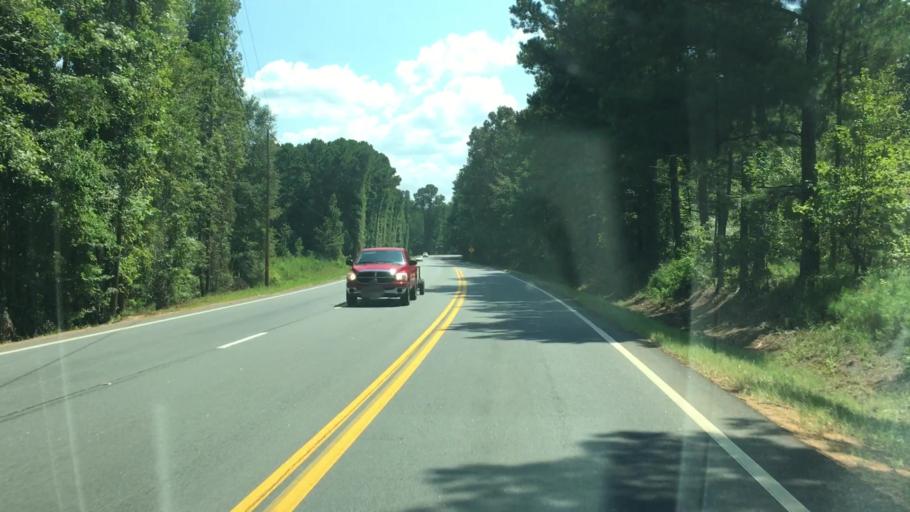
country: US
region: Georgia
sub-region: Oconee County
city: Watkinsville
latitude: 33.7309
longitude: -83.4307
